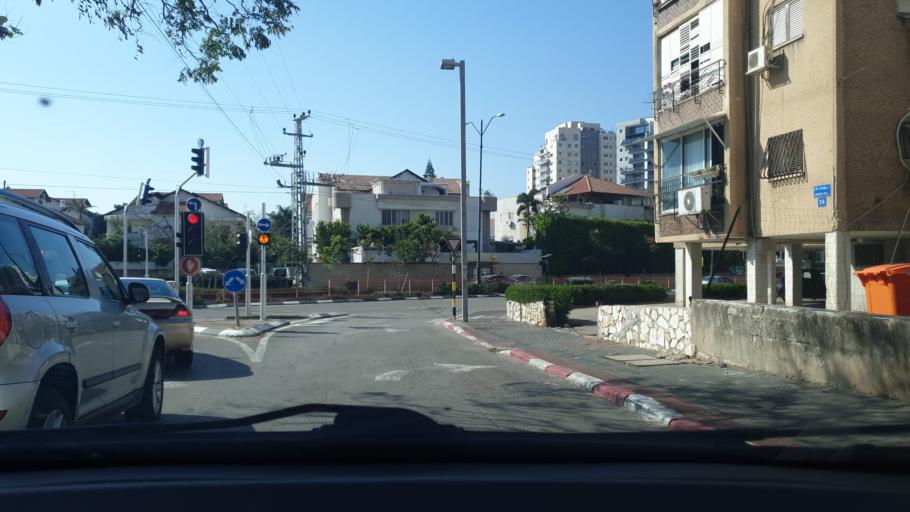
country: IL
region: Central District
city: Rishon LeZiyyon
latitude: 31.9704
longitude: 34.7991
